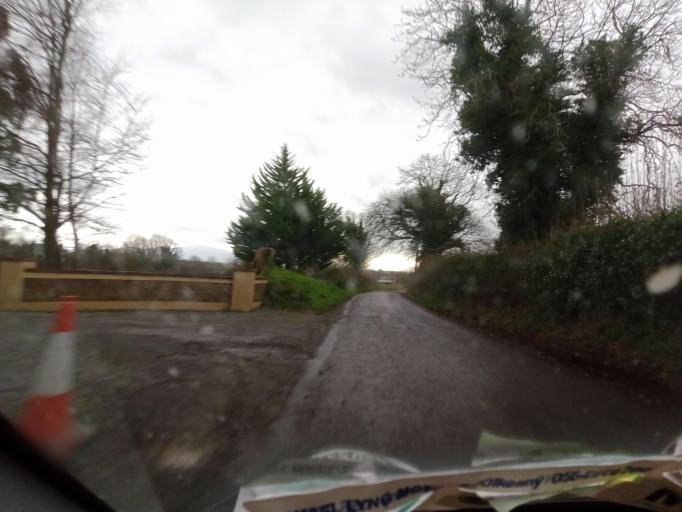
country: IE
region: Munster
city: Fethard
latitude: 52.5201
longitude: -7.7576
